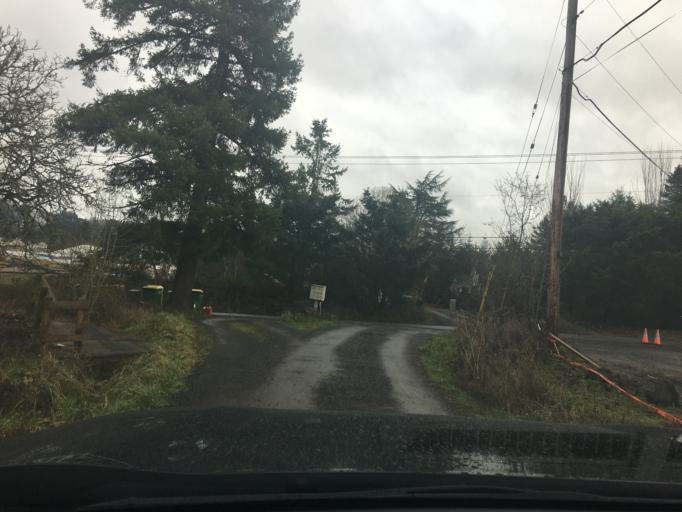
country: US
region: Oregon
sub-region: Washington County
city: Oak Hills
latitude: 45.5724
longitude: -122.8385
